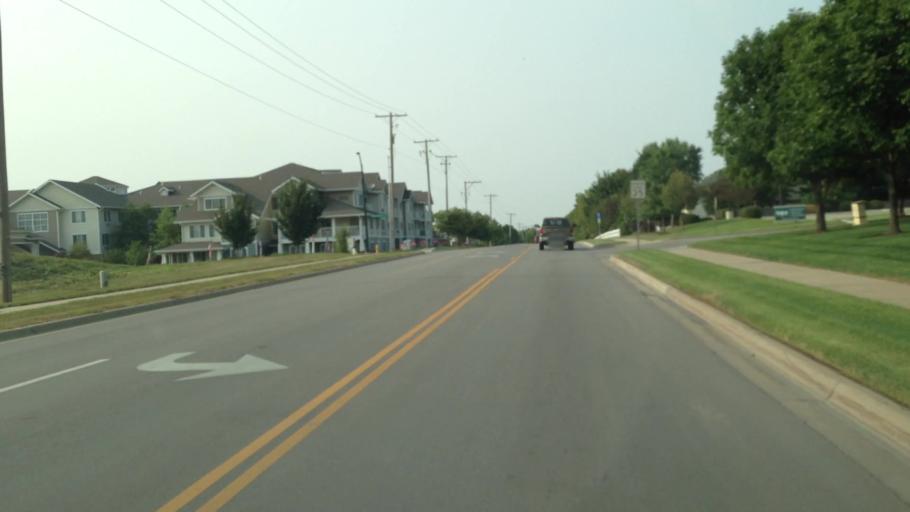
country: US
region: Kansas
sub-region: Douglas County
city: Lawrence
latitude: 38.9718
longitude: -95.2975
